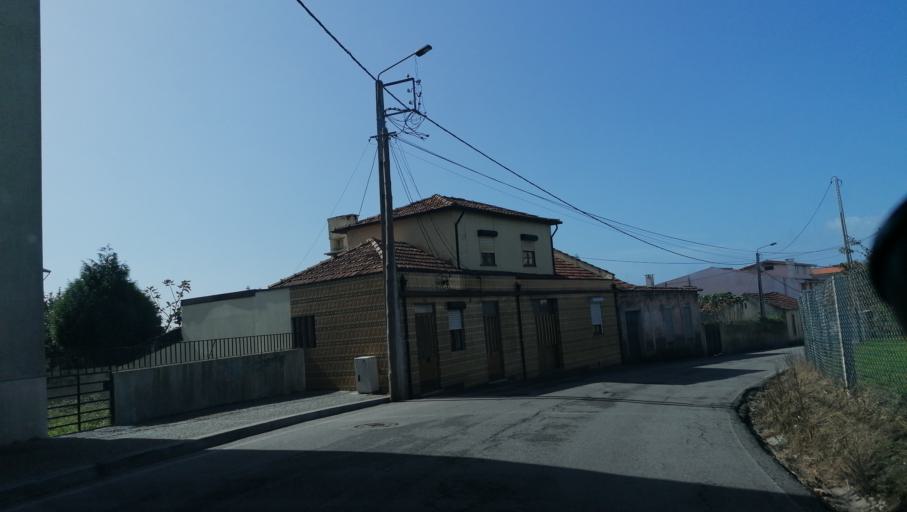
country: PT
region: Aveiro
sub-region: Espinho
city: Silvalde
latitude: 41.0061
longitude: -8.6285
